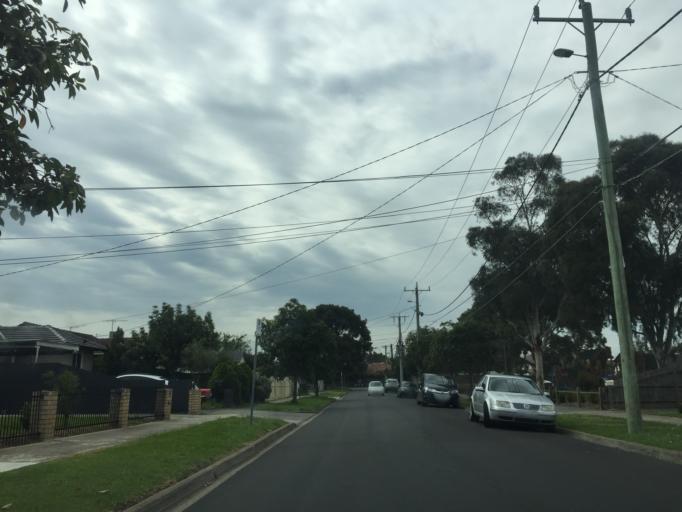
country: AU
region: Victoria
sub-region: Darebin
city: Preston
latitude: -37.7455
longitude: 145.0171
